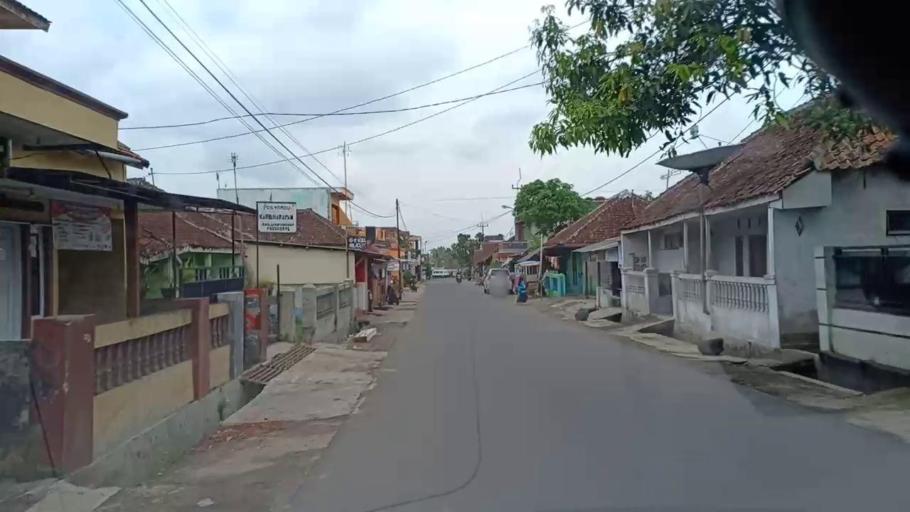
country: ID
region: West Java
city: Lemburwarung
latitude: -7.3374
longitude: 108.2696
